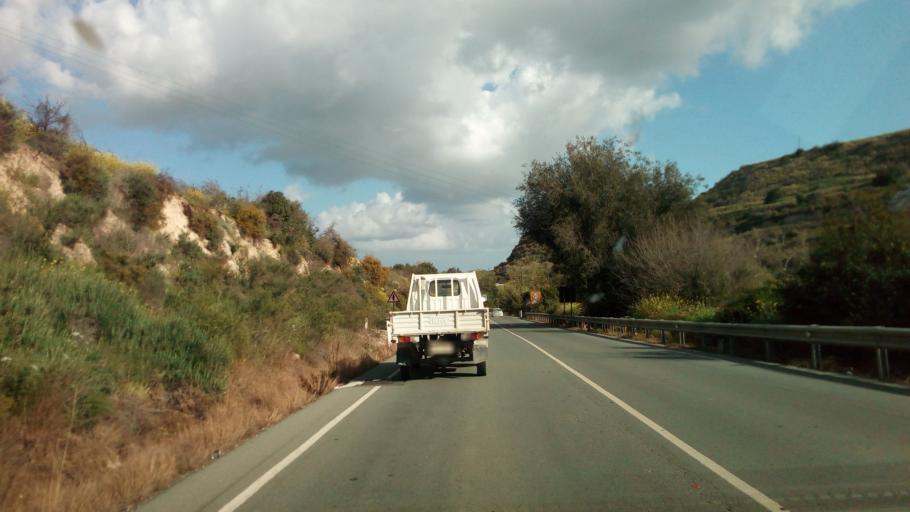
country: CY
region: Pafos
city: Polis
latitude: 34.9749
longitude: 32.4505
